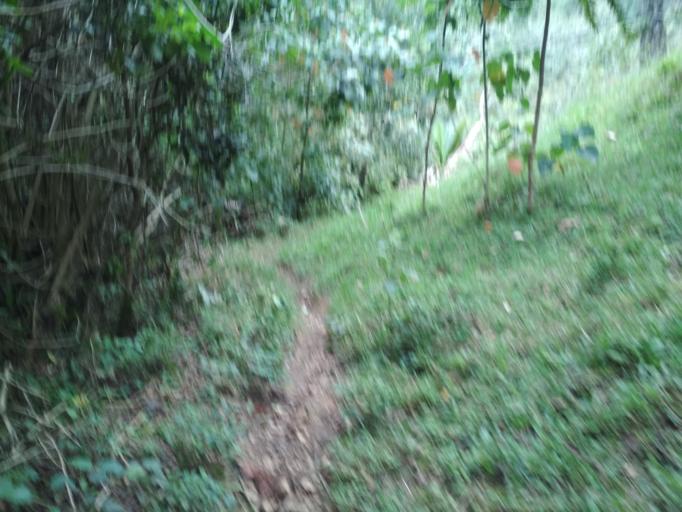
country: CO
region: Cauca
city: Totoro
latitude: 2.5323
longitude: -76.4211
